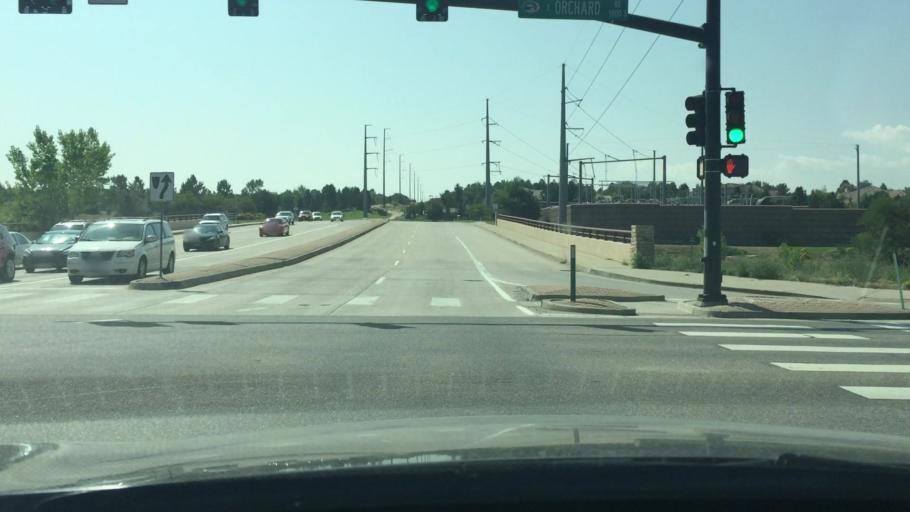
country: US
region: Colorado
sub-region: Arapahoe County
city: Dove Valley
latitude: 39.6106
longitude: -104.7918
